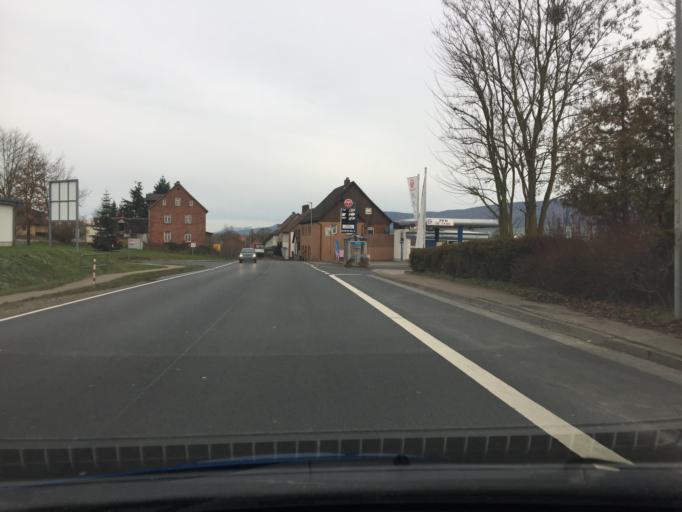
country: DE
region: Lower Saxony
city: Eschershausen
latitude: 51.9345
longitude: 9.6342
